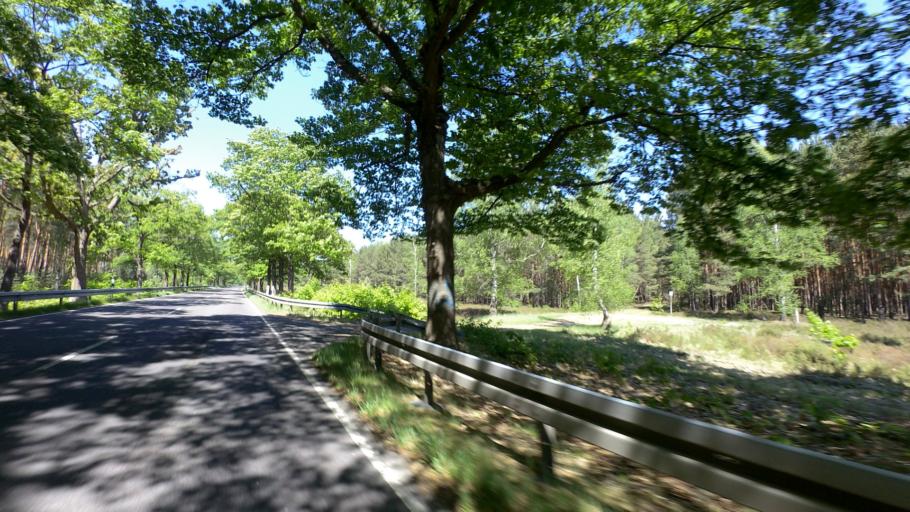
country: DE
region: Brandenburg
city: Drachhausen
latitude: 51.9130
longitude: 14.3515
